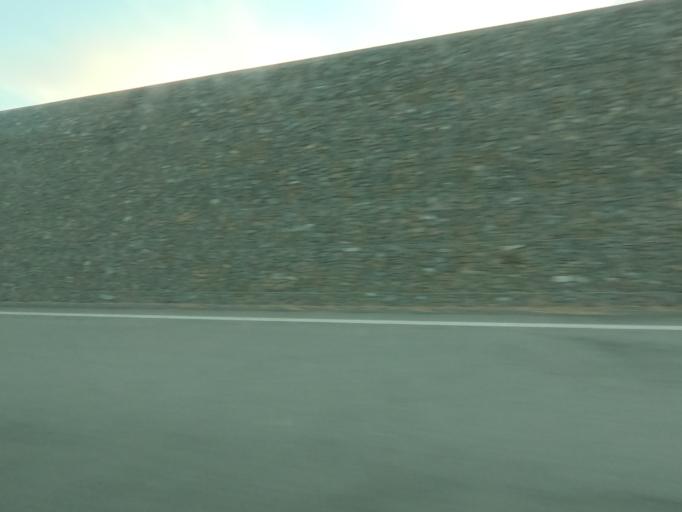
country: PT
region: Vila Real
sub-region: Peso da Regua
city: Peso da Regua
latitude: 41.1805
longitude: -7.7506
